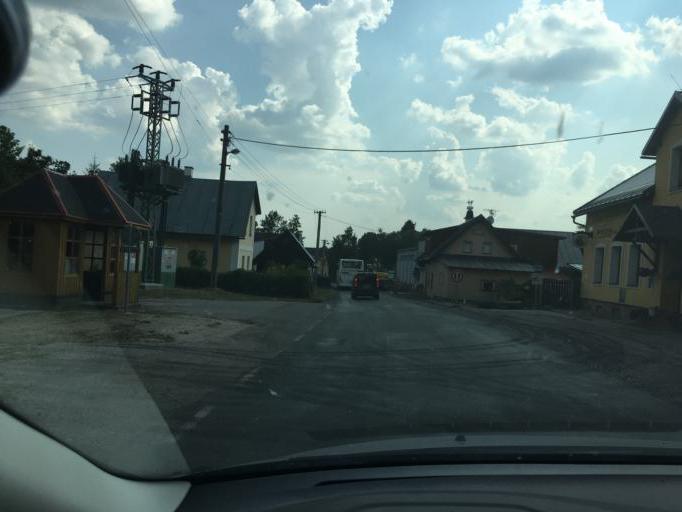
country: CZ
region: Kralovehradecky
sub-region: Okres Trutnov
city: Rudnik
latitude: 50.6152
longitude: 15.7073
